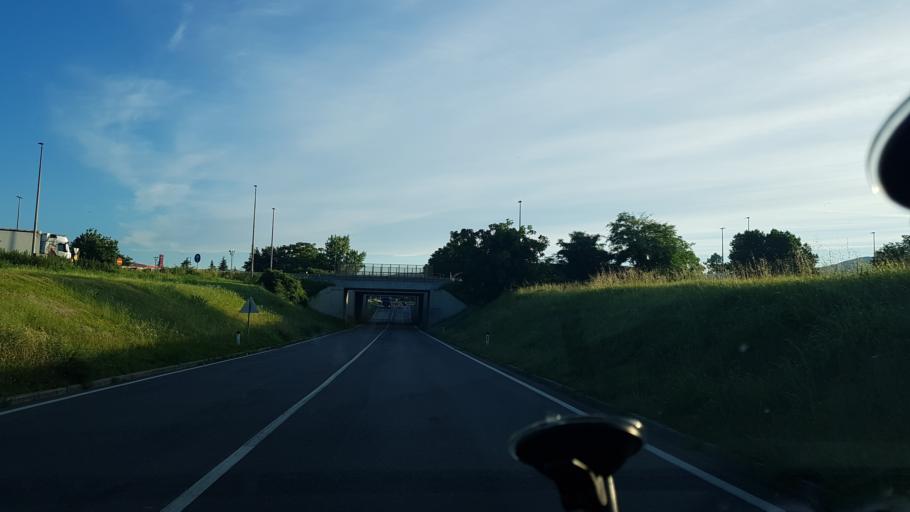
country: SI
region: Sempeter-Vrtojba
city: Vrtojba
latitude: 45.9189
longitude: 13.6296
